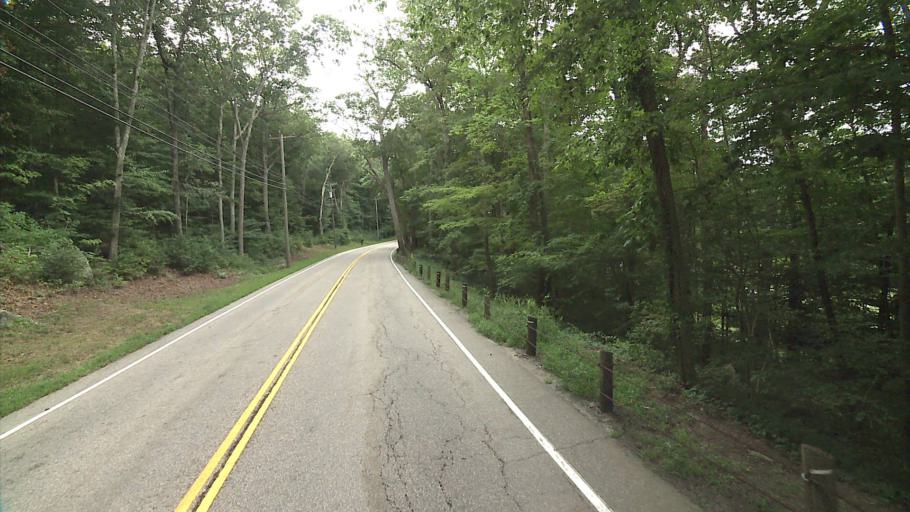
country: US
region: Connecticut
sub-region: Middlesex County
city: Essex Village
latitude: 41.4068
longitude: -72.3399
